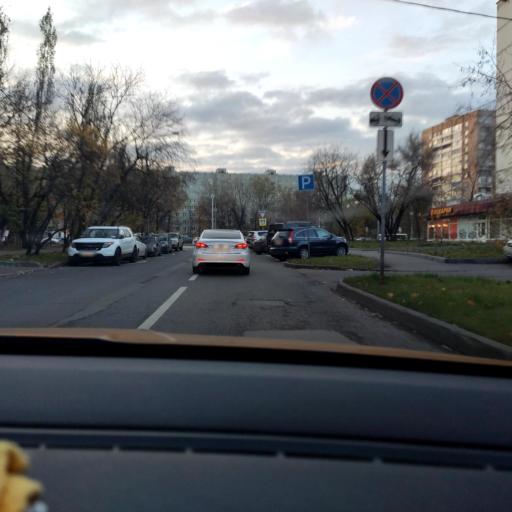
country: RU
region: Moscow
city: Gol'yanovo
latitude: 55.8129
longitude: 37.8209
